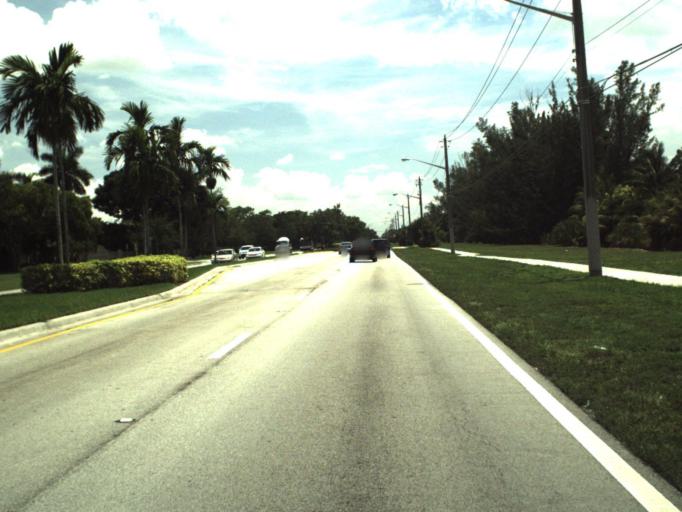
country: US
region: Florida
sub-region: Broward County
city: Coral Springs
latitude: 26.2844
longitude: -80.2504
